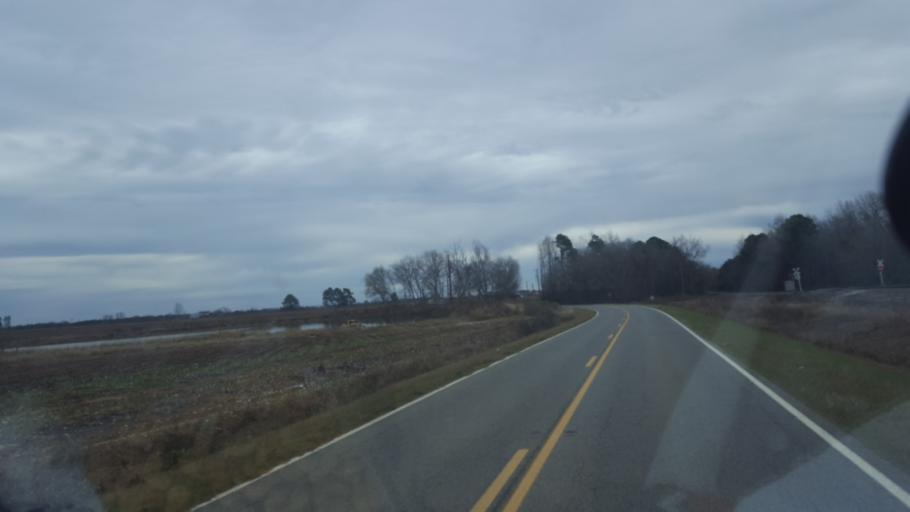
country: US
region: Georgia
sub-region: Ben Hill County
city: Fitzgerald
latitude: 31.7446
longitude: -83.3202
